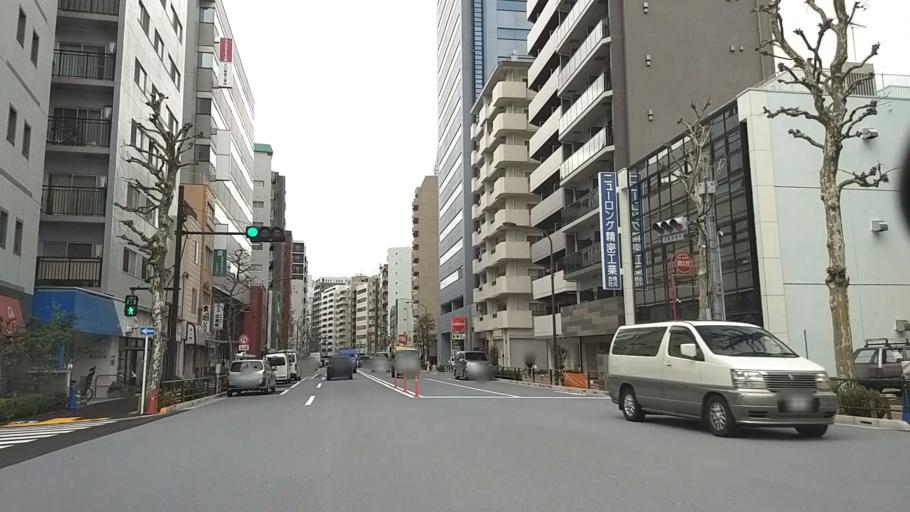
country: JP
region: Tokyo
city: Tokyo
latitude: 35.6247
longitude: 139.7316
